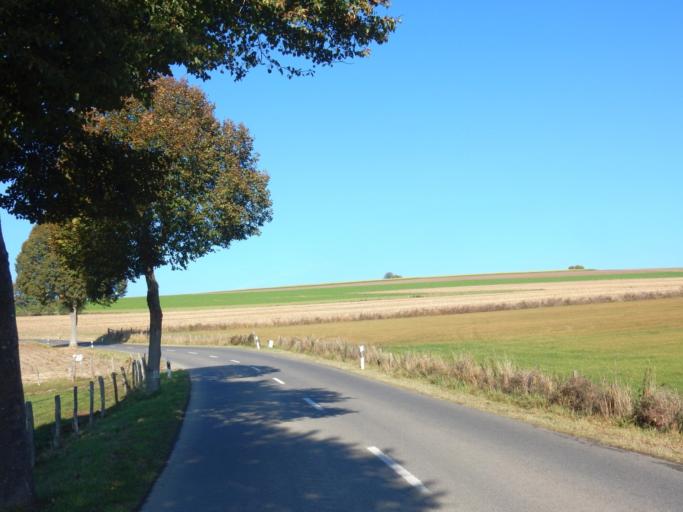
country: LU
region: Diekirch
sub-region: Canton de Clervaux
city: Troisvierges
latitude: 50.1357
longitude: 5.9925
